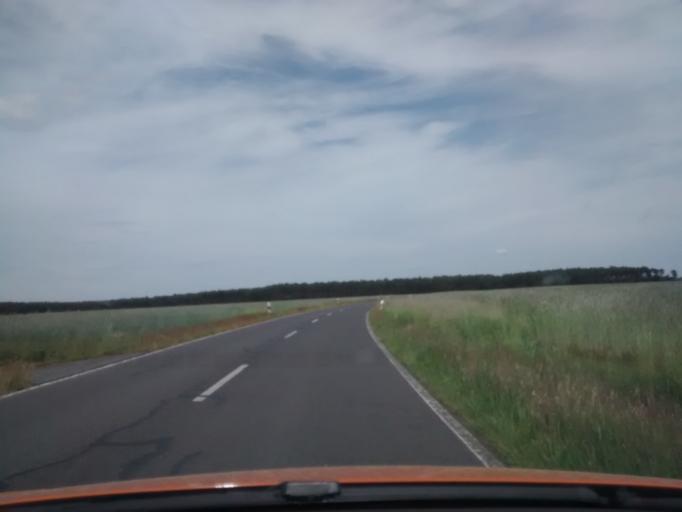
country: DE
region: Brandenburg
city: Ihlow
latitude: 51.8489
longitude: 13.2757
